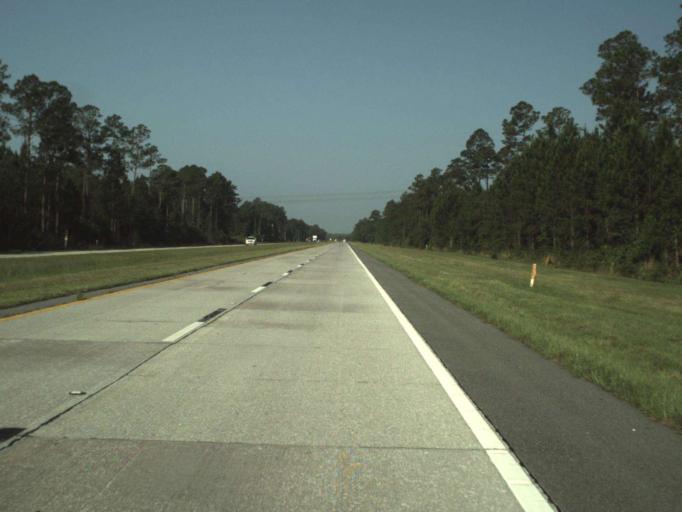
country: US
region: Florida
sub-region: Volusia County
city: North DeLand
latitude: 29.1088
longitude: -81.2001
